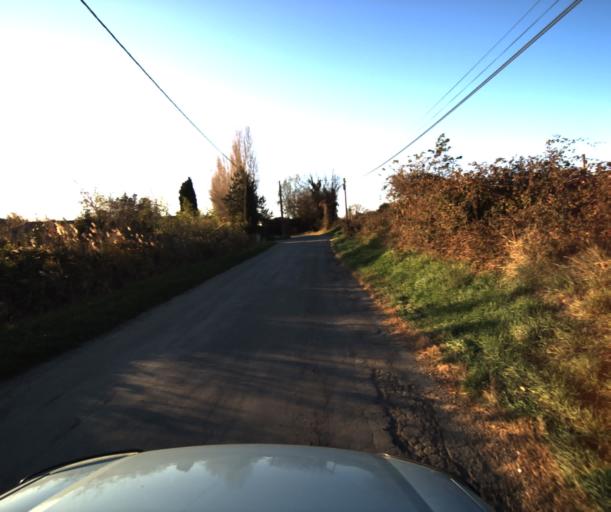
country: FR
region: Provence-Alpes-Cote d'Azur
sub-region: Departement du Vaucluse
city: Pertuis
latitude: 43.6807
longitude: 5.5135
